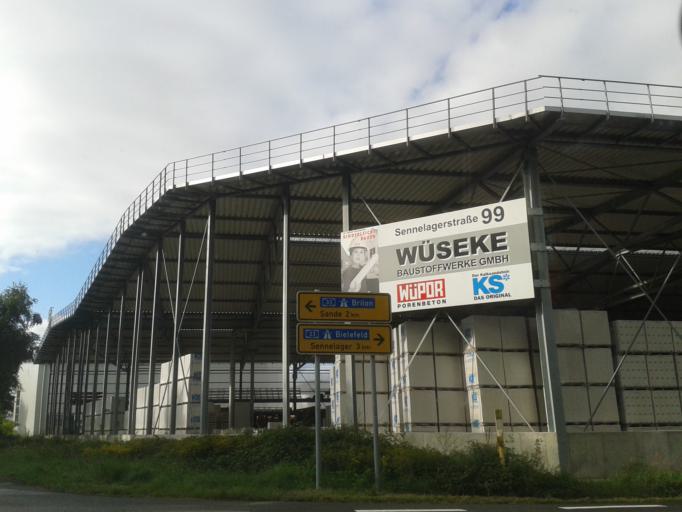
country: DE
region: North Rhine-Westphalia
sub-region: Regierungsbezirk Detmold
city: Hovelhof
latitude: 51.7654
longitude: 8.6897
